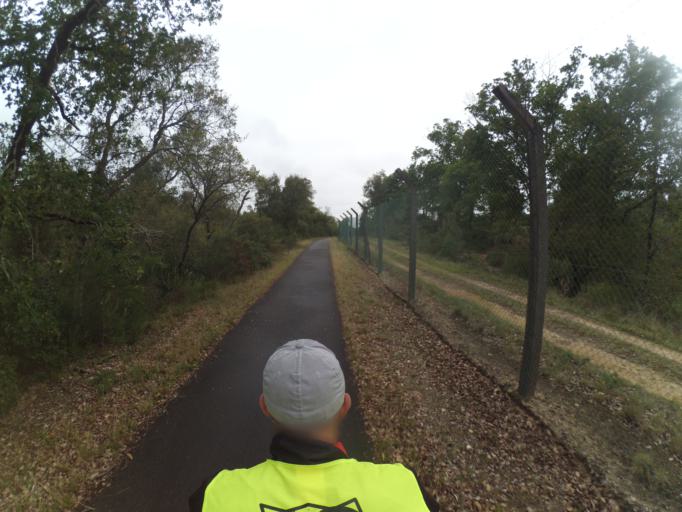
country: FR
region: Aquitaine
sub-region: Departement des Landes
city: Mimizan
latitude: 44.2232
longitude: -1.2658
